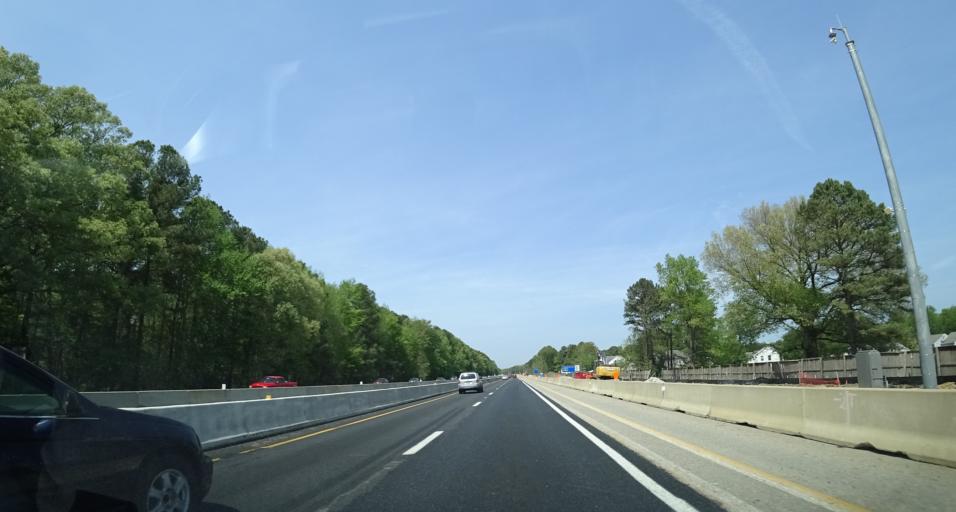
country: US
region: Virginia
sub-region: York County
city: Yorktown
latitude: 37.1457
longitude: -76.5327
